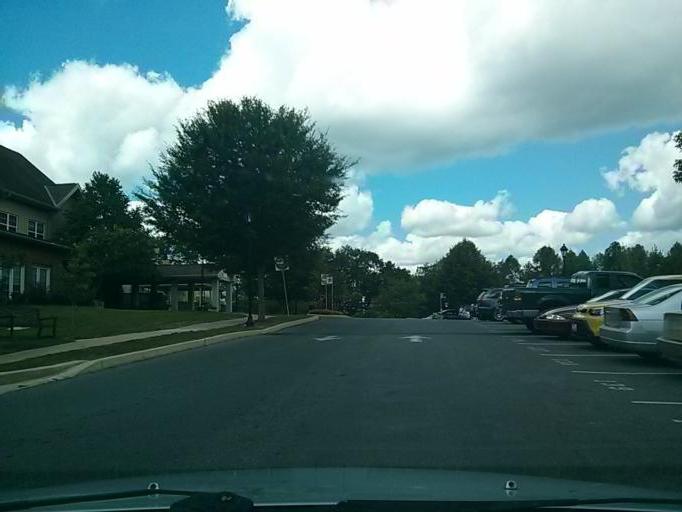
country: US
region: Pennsylvania
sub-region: Centre County
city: State College
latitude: 40.8251
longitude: -77.8728
